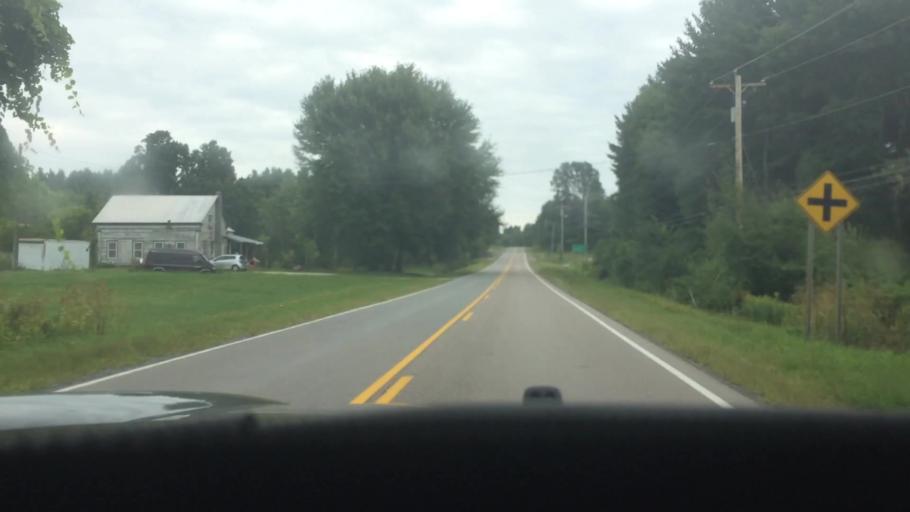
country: US
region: New York
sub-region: St. Lawrence County
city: Hannawa Falls
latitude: 44.5377
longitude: -75.0208
